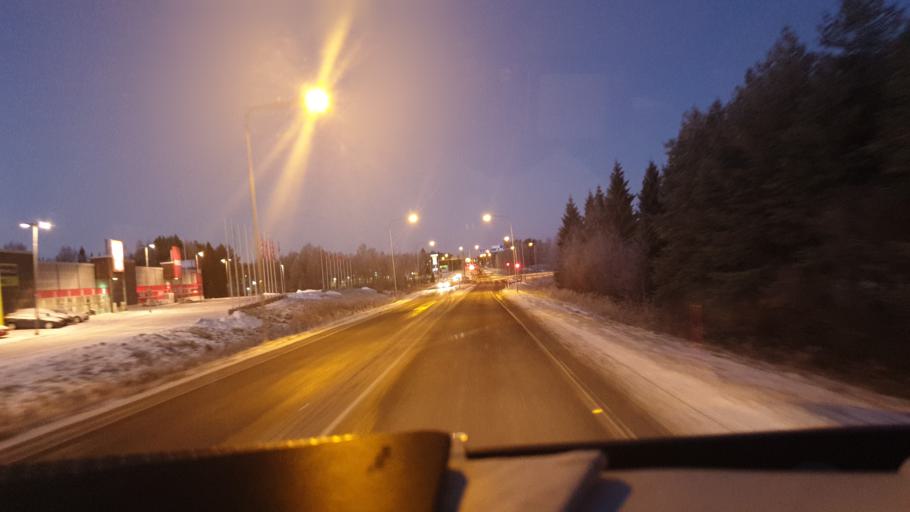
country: FI
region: Northern Ostrobothnia
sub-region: Raahe
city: Raahe
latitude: 64.6868
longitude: 24.5735
